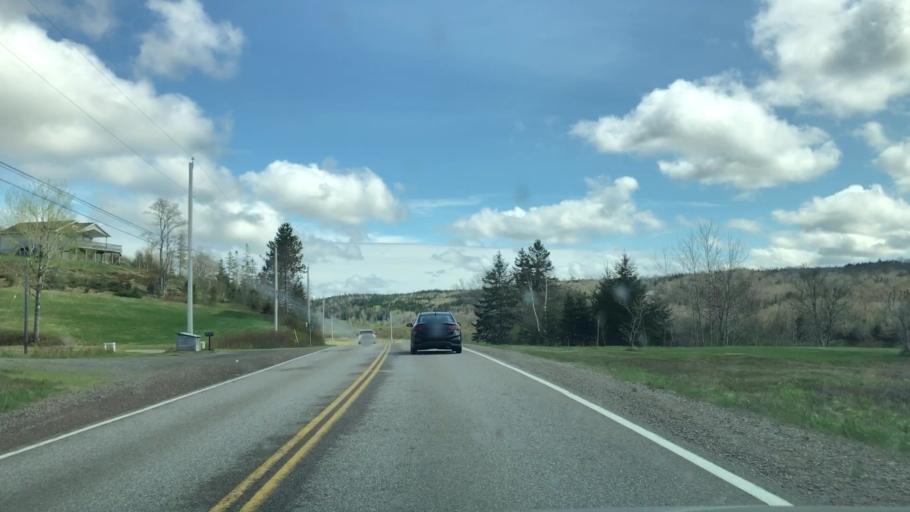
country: CA
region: Nova Scotia
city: Antigonish
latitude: 45.1980
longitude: -62.0023
